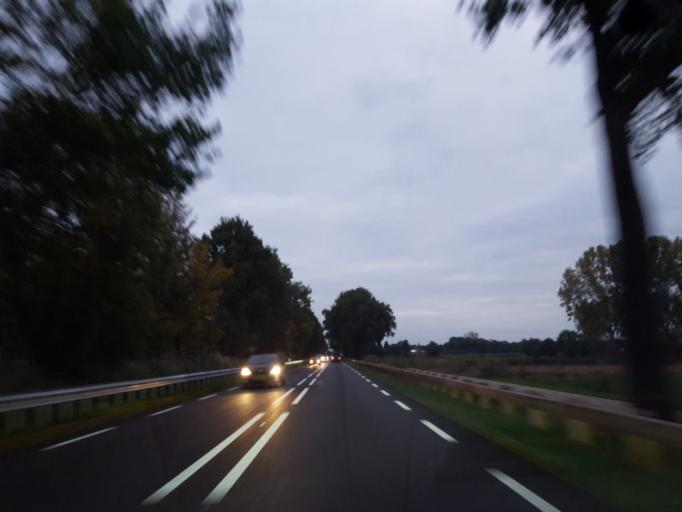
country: NL
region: North Brabant
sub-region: Gemeente Someren
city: Someren
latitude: 51.3713
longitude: 5.7394
